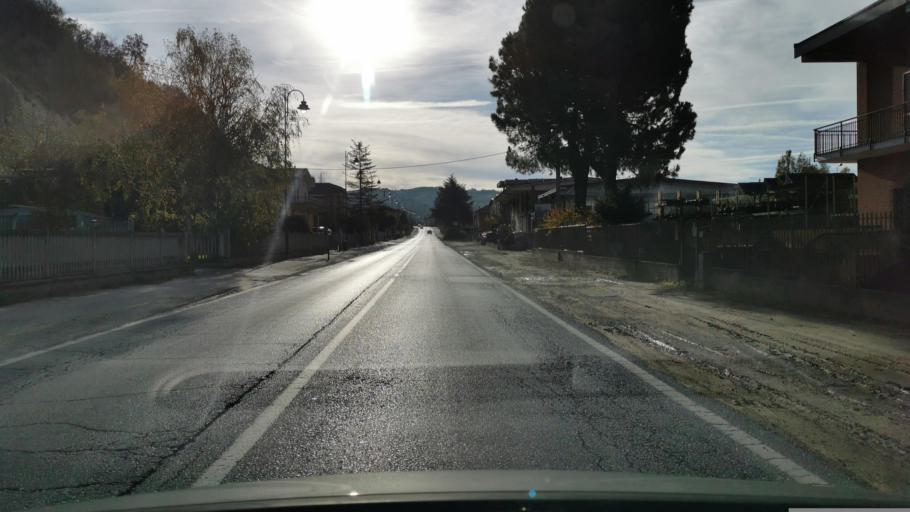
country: IT
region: Piedmont
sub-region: Provincia di Cuneo
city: Dogliani
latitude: 44.5401
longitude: 7.9304
